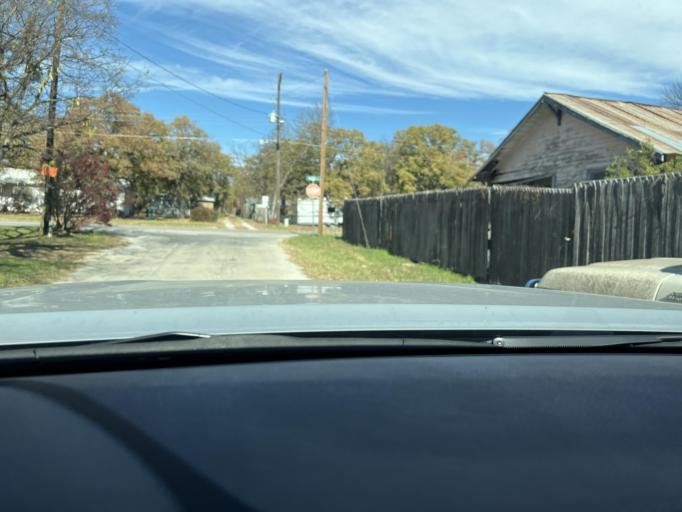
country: US
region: Texas
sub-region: Eastland County
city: Eastland
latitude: 32.3887
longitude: -98.8190
